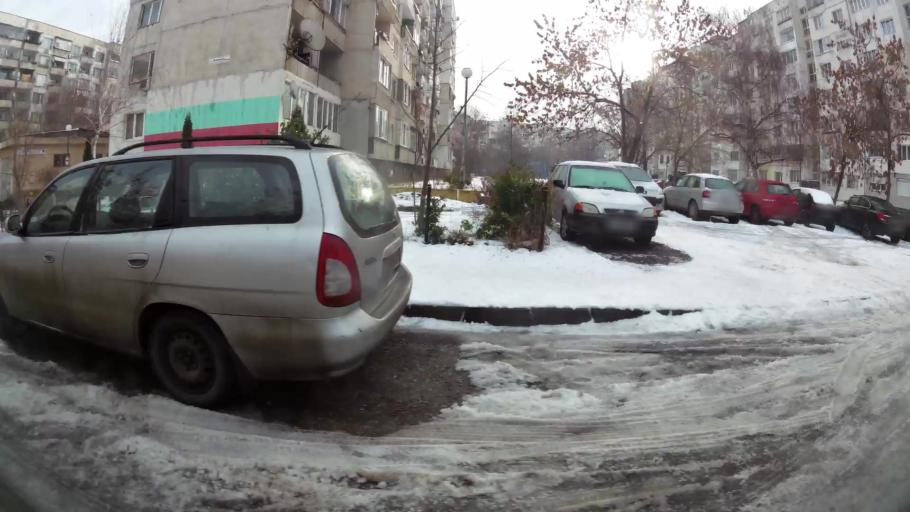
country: BG
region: Sofia-Capital
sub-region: Stolichna Obshtina
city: Sofia
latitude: 42.7097
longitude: 23.2983
